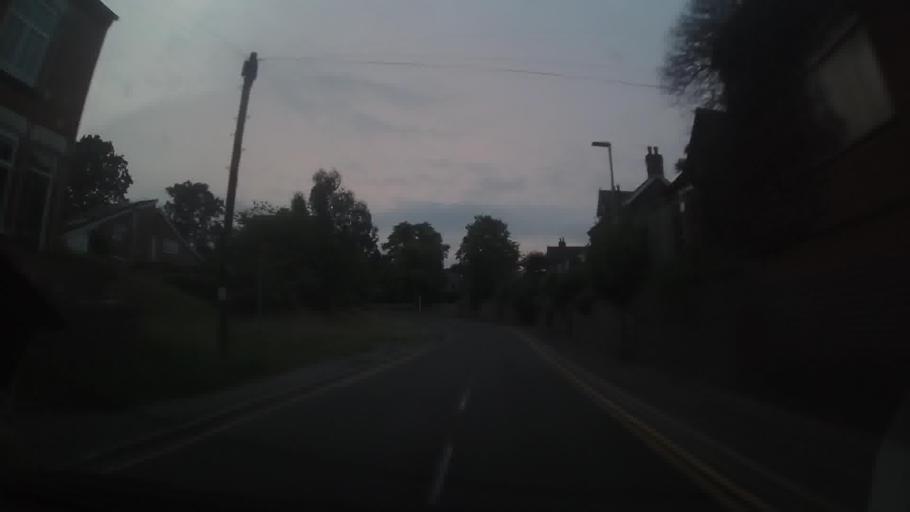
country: GB
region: England
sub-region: Leicestershire
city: Mountsorrel
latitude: 52.7069
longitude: -1.1404
